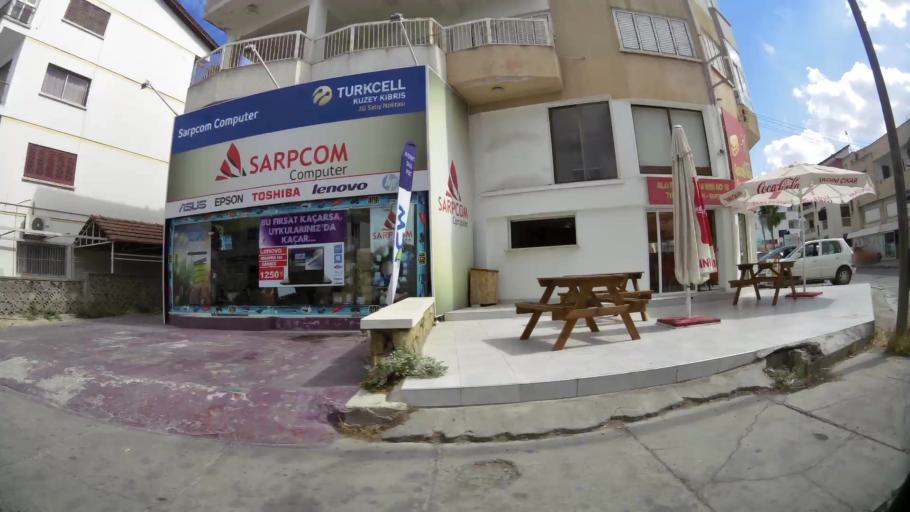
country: CY
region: Lefkosia
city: Nicosia
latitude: 35.1990
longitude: 33.3444
